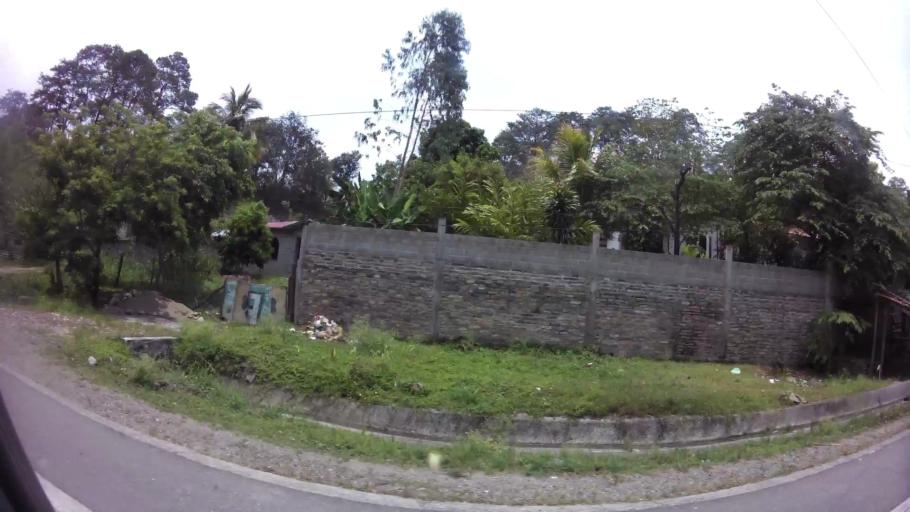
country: HN
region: Comayagua
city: Taulabe
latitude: 14.6830
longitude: -87.9544
